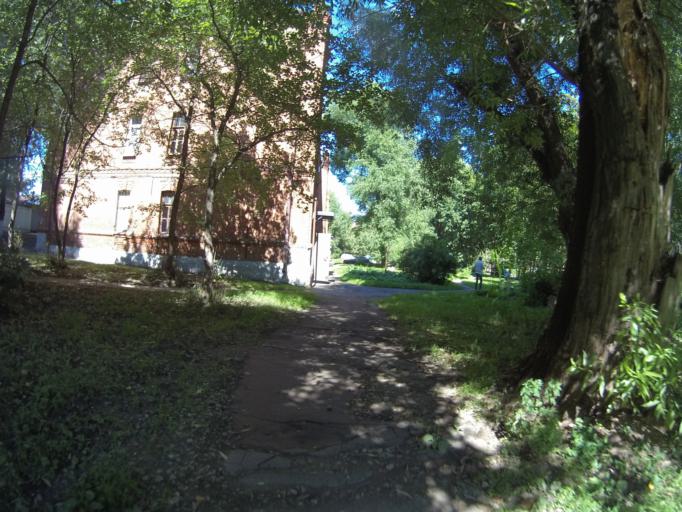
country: RU
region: Vladimir
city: Vladimir
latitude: 56.1332
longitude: 40.3701
